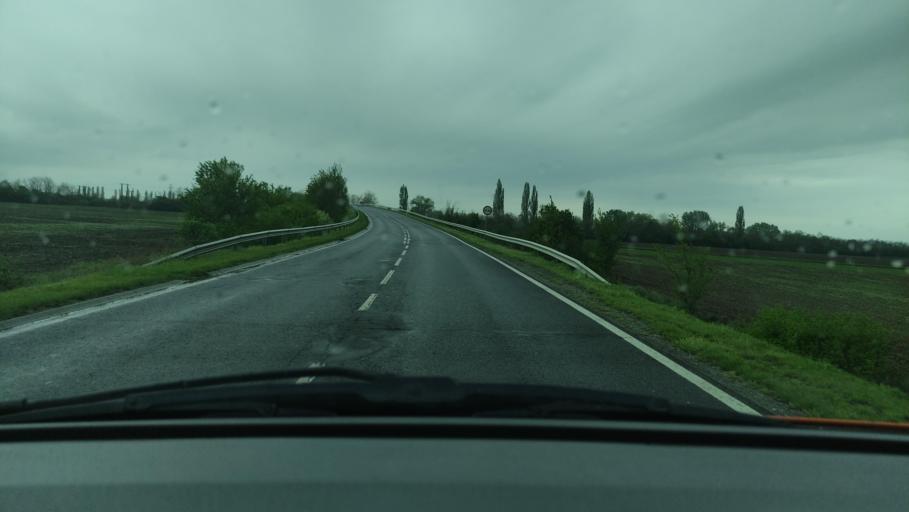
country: HU
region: Baranya
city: Mohacs
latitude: 45.9933
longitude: 18.6549
